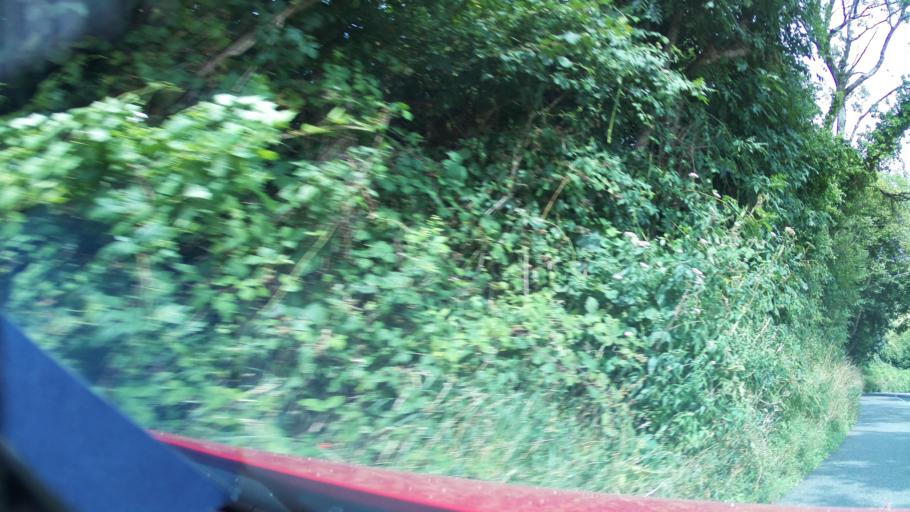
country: GB
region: England
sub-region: Devon
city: Dartmouth
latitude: 50.3613
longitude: -3.5616
